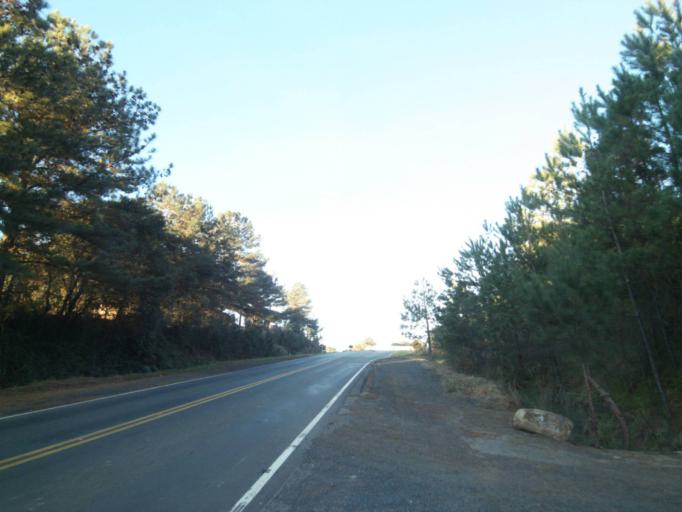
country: BR
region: Parana
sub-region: Tibagi
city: Tibagi
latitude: -24.5010
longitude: -50.4464
